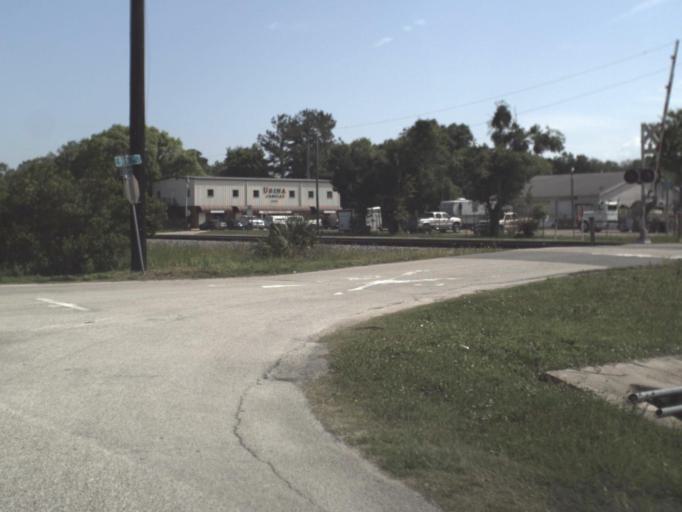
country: US
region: Florida
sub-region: Saint Johns County
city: Villano Beach
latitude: 29.9490
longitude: -81.3404
